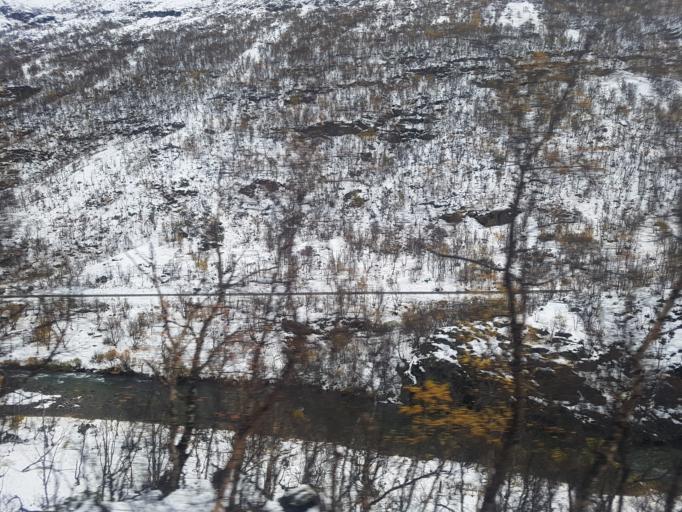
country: NO
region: Sor-Trondelag
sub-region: Oppdal
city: Oppdal
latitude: 62.3376
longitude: 9.6225
